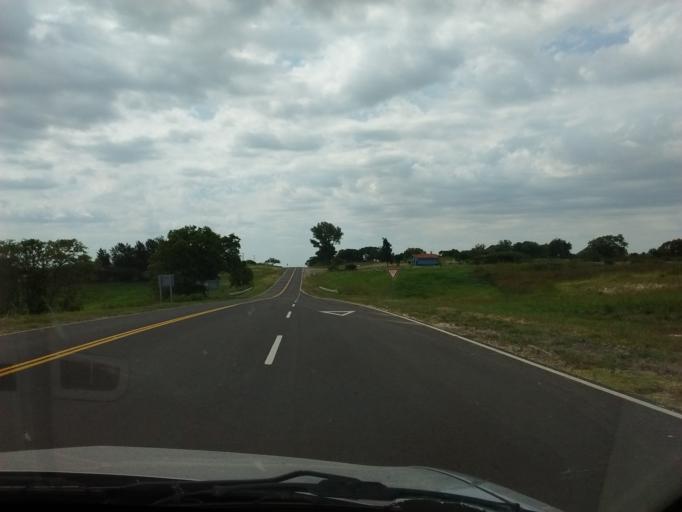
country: AR
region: Entre Rios
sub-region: Departamento de Victoria
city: Victoria
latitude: -32.8355
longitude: -59.8694
